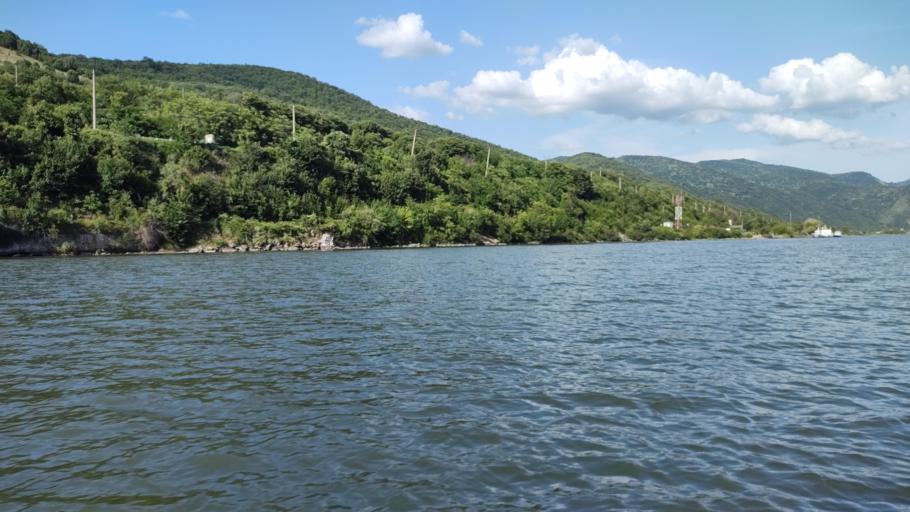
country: RO
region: Caras-Severin
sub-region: Comuna Berzasca
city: Berzasca
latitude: 44.6370
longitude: 21.9591
